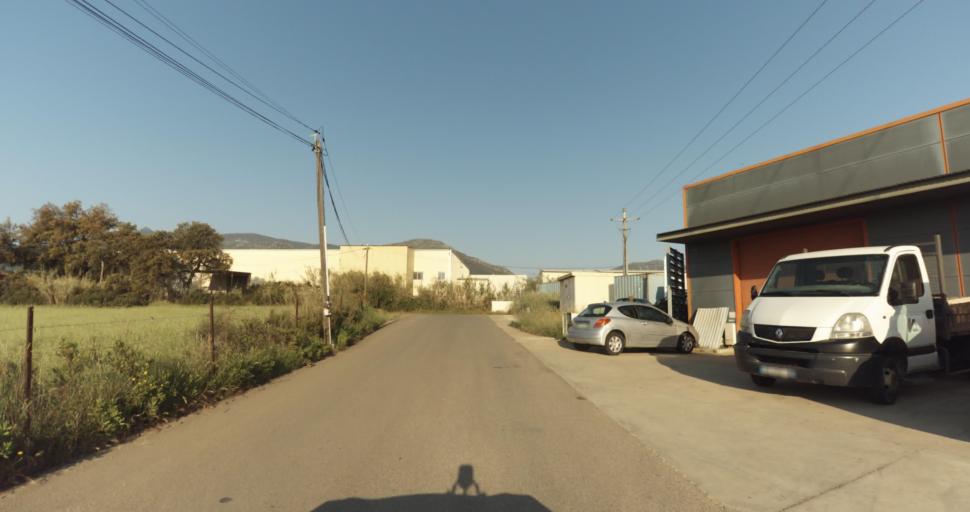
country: FR
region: Corsica
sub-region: Departement de la Haute-Corse
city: Biguglia
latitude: 42.5988
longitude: 9.4466
